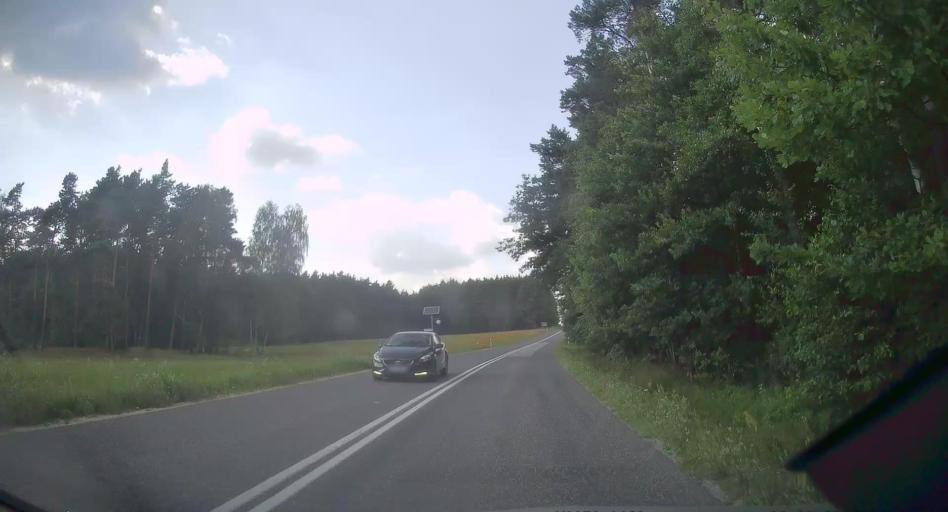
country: PL
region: Swietokrzyskie
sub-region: Powiat kielecki
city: Lopuszno
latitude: 50.8971
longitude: 20.2502
